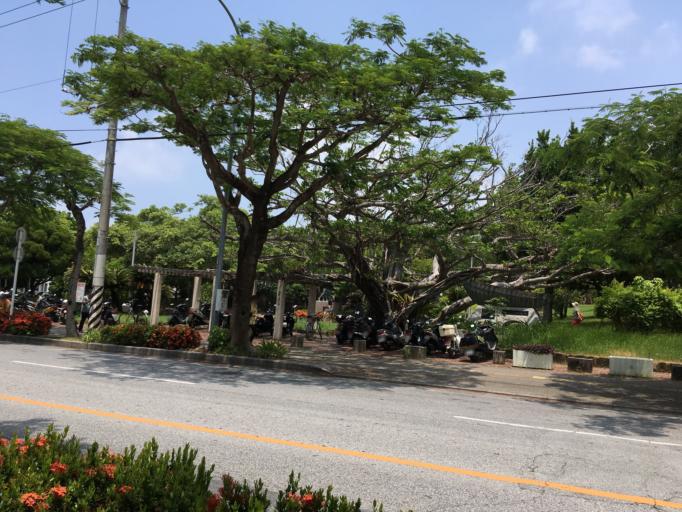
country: JP
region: Okinawa
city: Naha-shi
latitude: 26.2176
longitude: 127.6765
